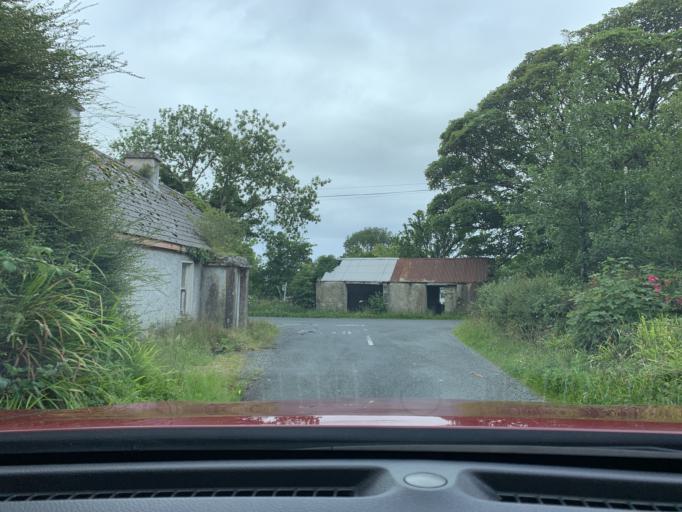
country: IE
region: Connaught
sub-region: County Leitrim
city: Kinlough
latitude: 54.4001
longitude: -8.4051
